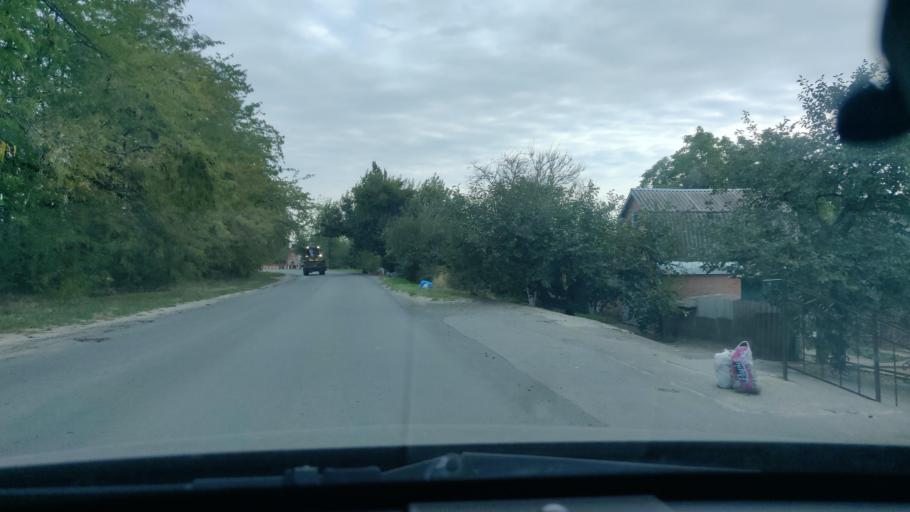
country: RU
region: Rostov
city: Ust'-Donetskiy
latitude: 47.6467
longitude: 40.8697
